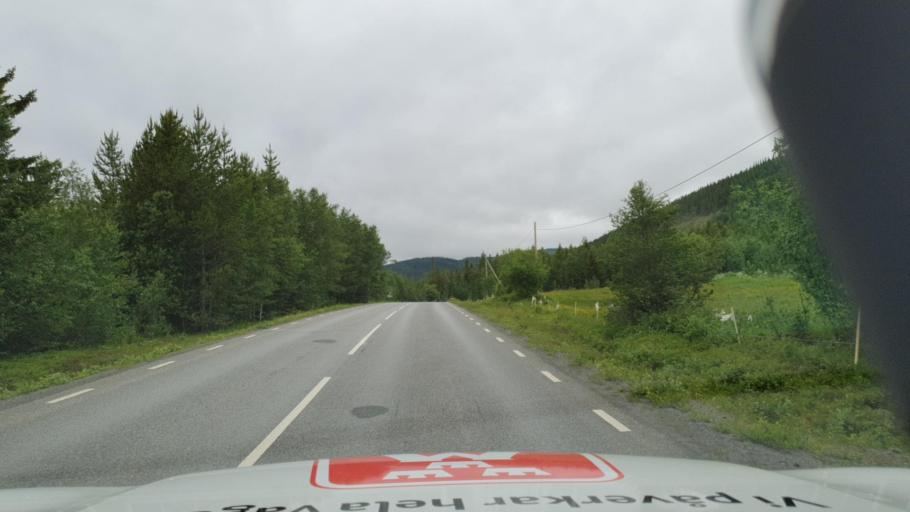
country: SE
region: Jaemtland
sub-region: Are Kommun
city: Are
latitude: 63.5121
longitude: 13.1347
